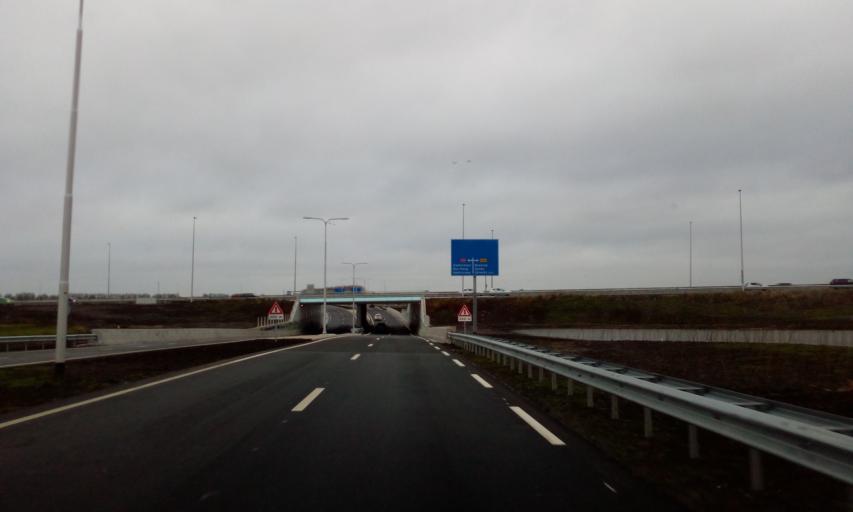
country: NL
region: South Holland
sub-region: Gemeente Waddinxveen
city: Waddinxveen
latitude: 52.0192
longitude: 4.6437
